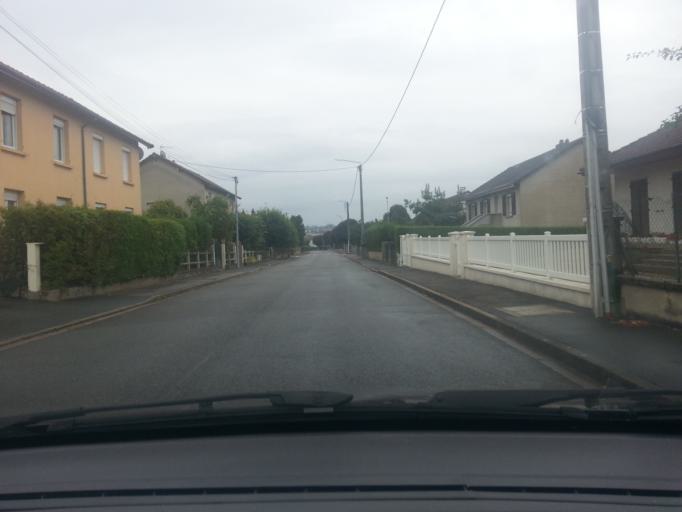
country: FR
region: Bourgogne
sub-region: Departement de Saone-et-Loire
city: Montchanin
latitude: 46.7419
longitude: 4.4703
